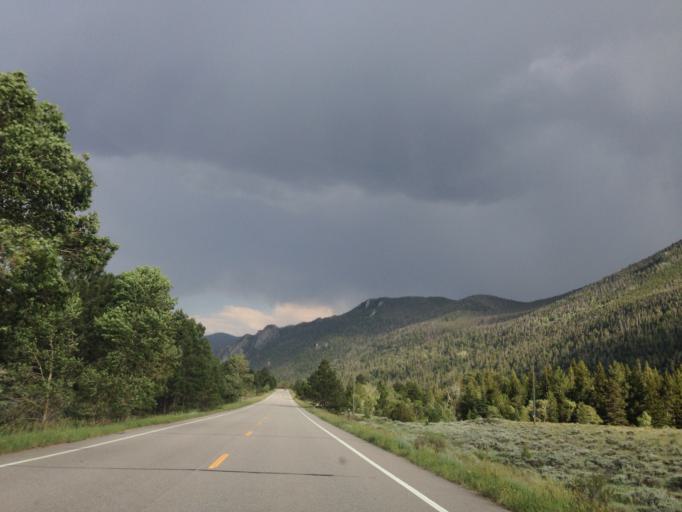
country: US
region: Colorado
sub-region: Larimer County
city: Estes Park
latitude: 40.7083
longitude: -105.7233
